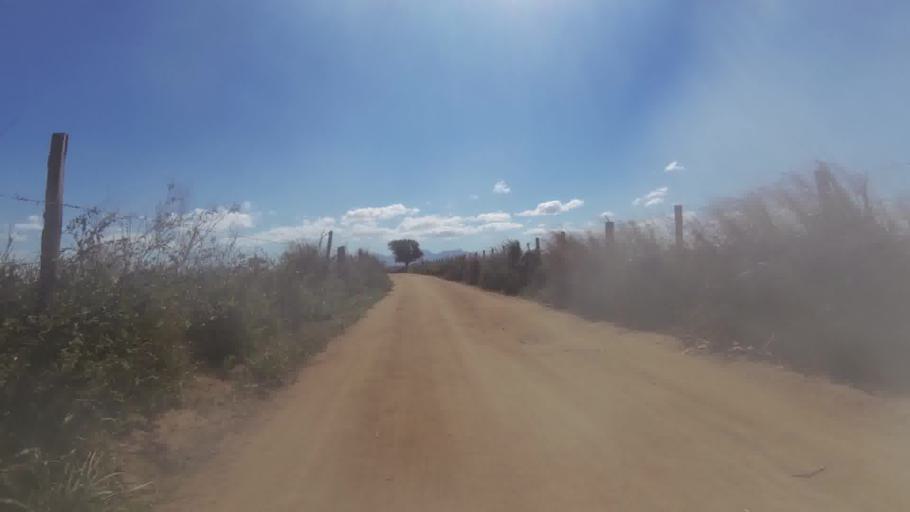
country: BR
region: Espirito Santo
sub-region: Marataizes
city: Marataizes
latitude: -21.1552
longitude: -40.9672
